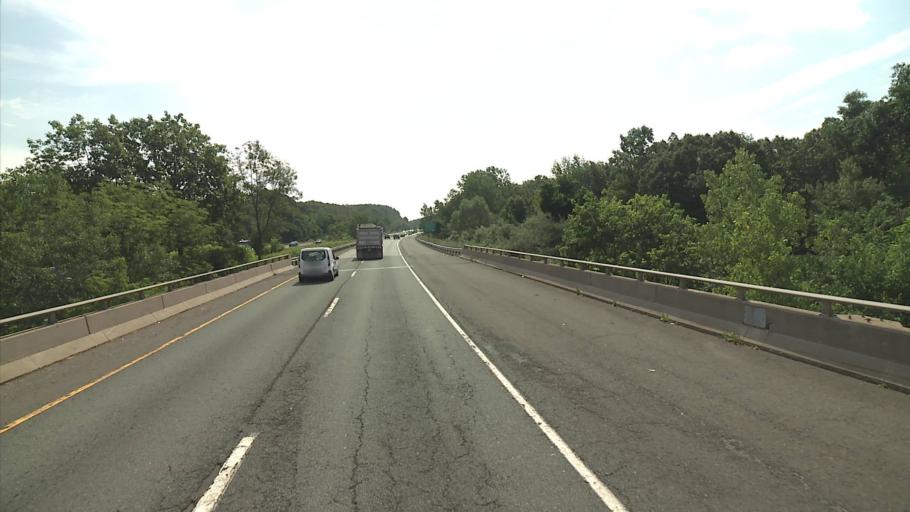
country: US
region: Connecticut
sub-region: New Haven County
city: Cheshire Village
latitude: 41.5553
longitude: -72.8718
